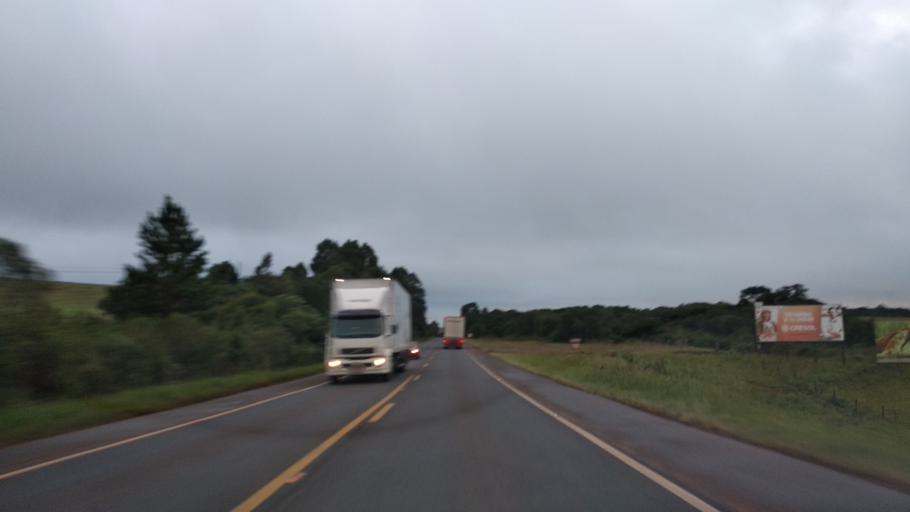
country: BR
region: Santa Catarina
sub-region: Campos Novos
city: Campos Novos
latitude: -27.3812
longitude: -51.0996
